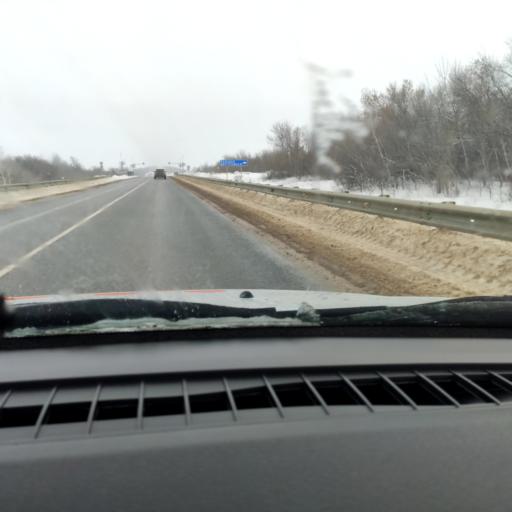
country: RU
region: Samara
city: Dubovyy Umet
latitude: 52.5615
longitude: 50.4892
